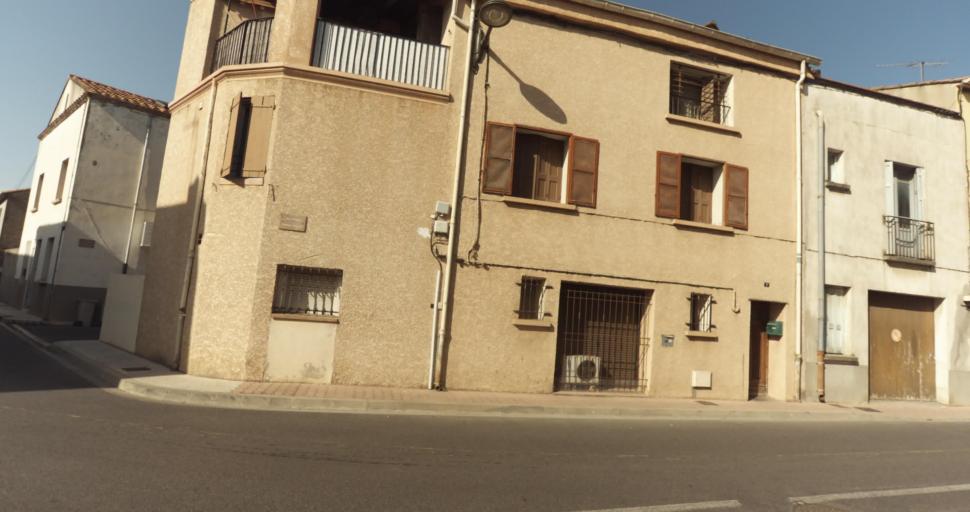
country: FR
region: Languedoc-Roussillon
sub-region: Departement des Pyrenees-Orientales
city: Alenya
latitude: 42.6380
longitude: 2.9815
